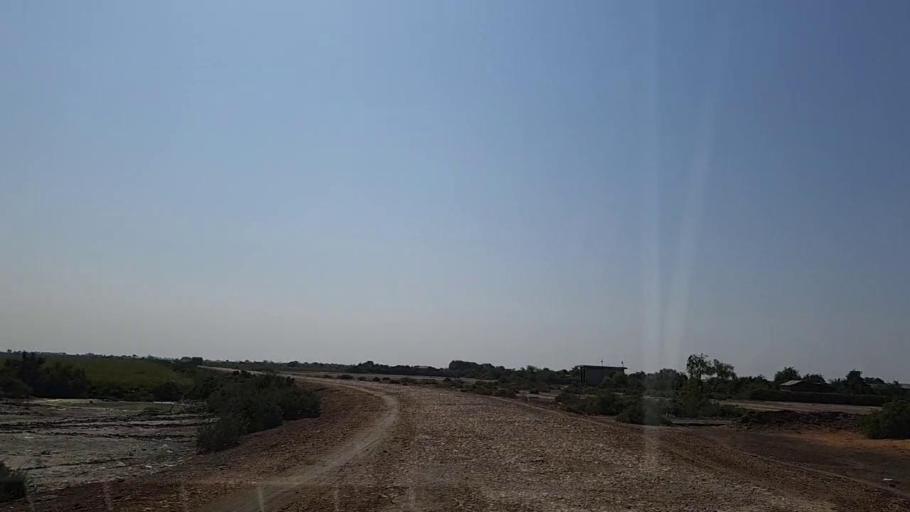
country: PK
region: Sindh
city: Chuhar Jamali
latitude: 24.4742
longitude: 68.0911
